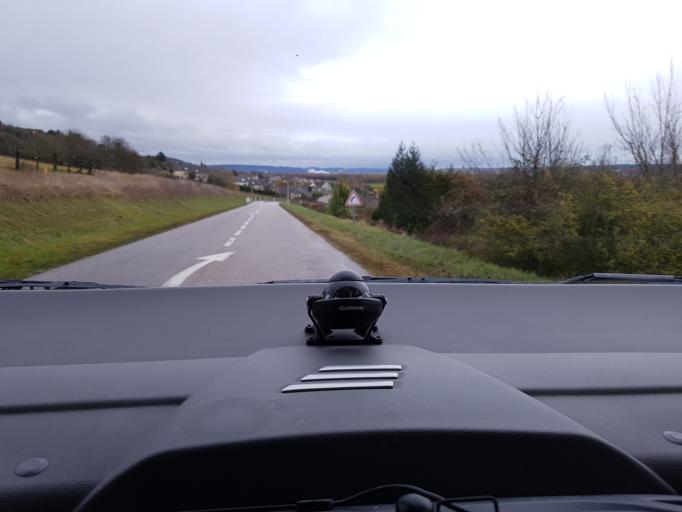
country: FR
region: Haute-Normandie
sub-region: Departement de la Seine-Maritime
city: Tourville-la-Riviere
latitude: 49.3192
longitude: 1.1106
